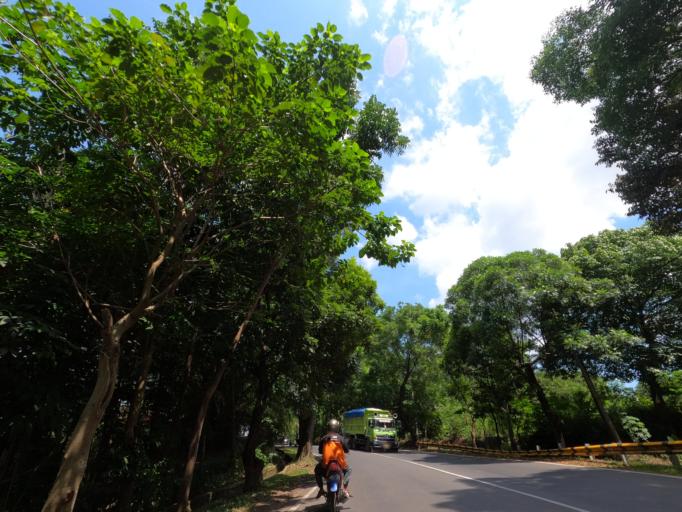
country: ID
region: West Java
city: Pamanukan
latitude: -6.5539
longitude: 107.7467
